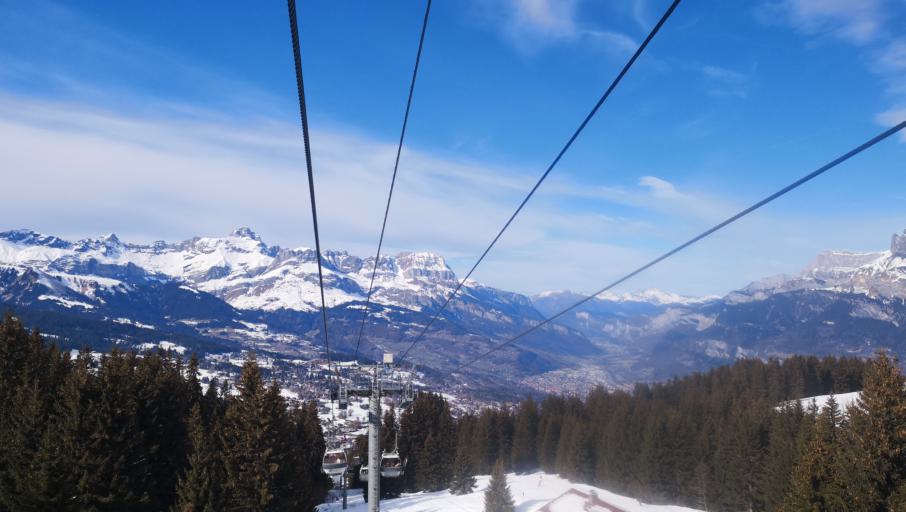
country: FR
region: Rhone-Alpes
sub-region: Departement de la Haute-Savoie
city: Combloux
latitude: 45.8661
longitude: 6.6561
